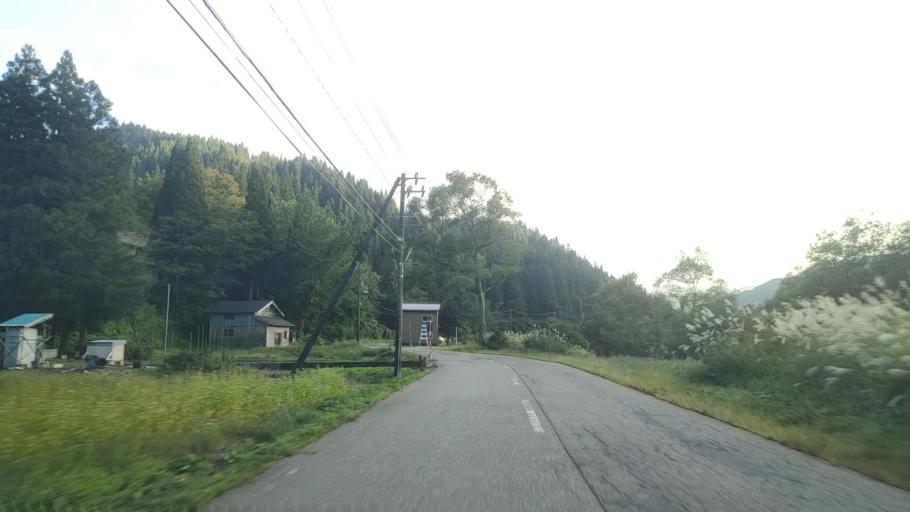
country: JP
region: Toyama
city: Yatsuomachi-higashikumisaka
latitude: 36.4675
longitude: 137.0481
